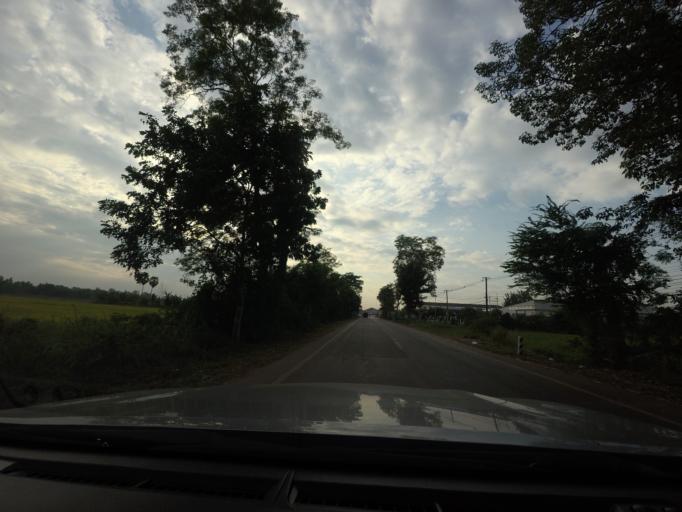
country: TH
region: Phitsanulok
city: Noen Maprang
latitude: 16.5692
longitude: 100.6473
